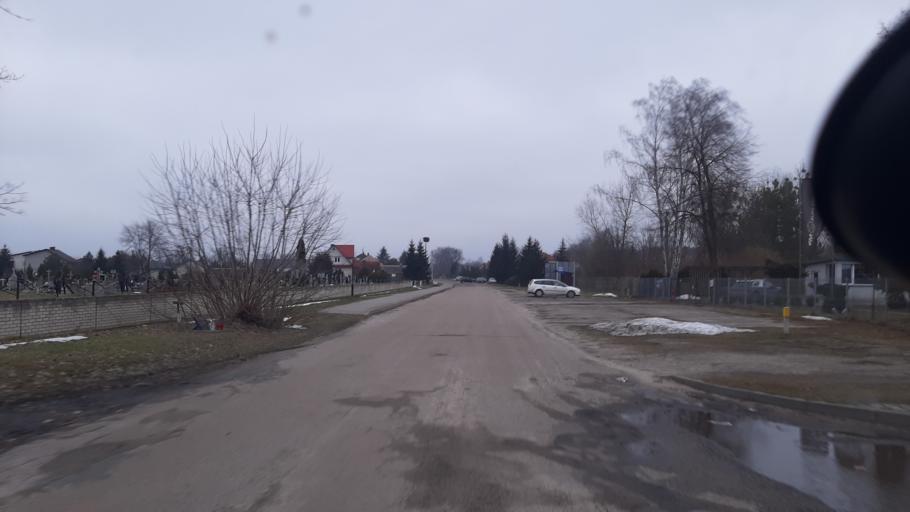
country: PL
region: Lublin Voivodeship
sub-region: Powiat wlodawski
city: Wlodawa
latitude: 51.5217
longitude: 23.5808
